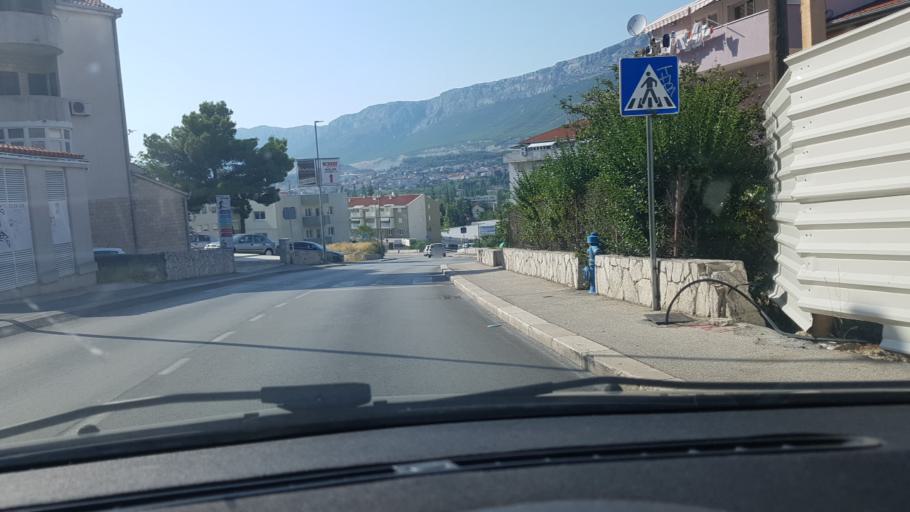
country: HR
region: Splitsko-Dalmatinska
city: Solin
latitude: 43.5315
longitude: 16.4921
